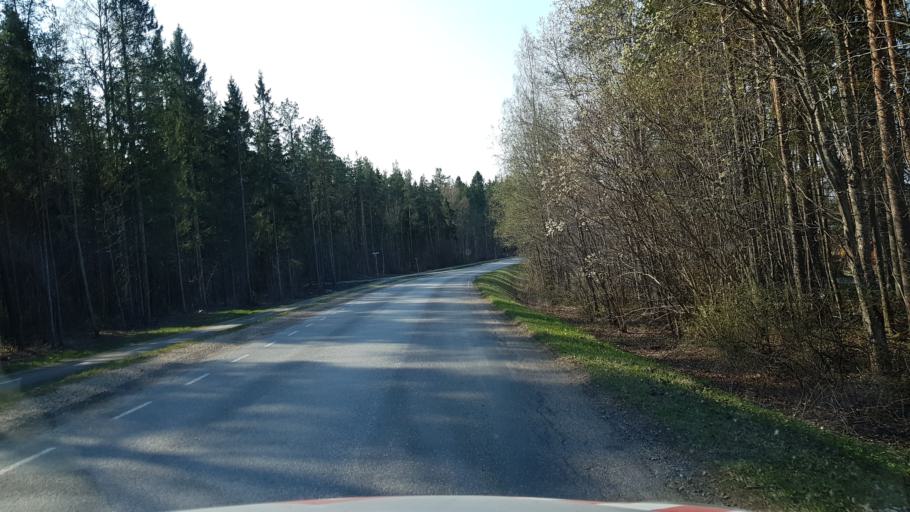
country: EE
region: Raplamaa
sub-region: Kohila vald
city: Kohila
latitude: 59.1752
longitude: 24.6562
